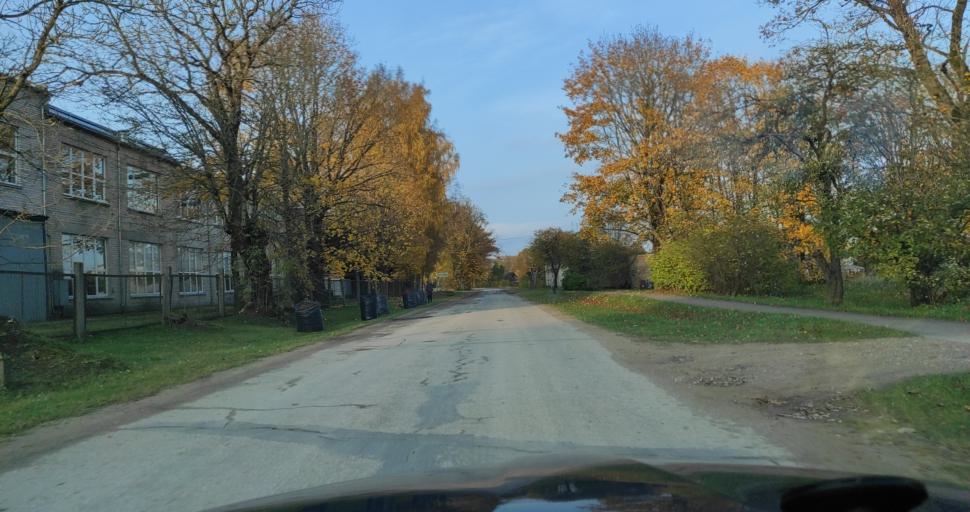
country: LV
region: Vainode
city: Vainode
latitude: 56.4310
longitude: 21.8706
